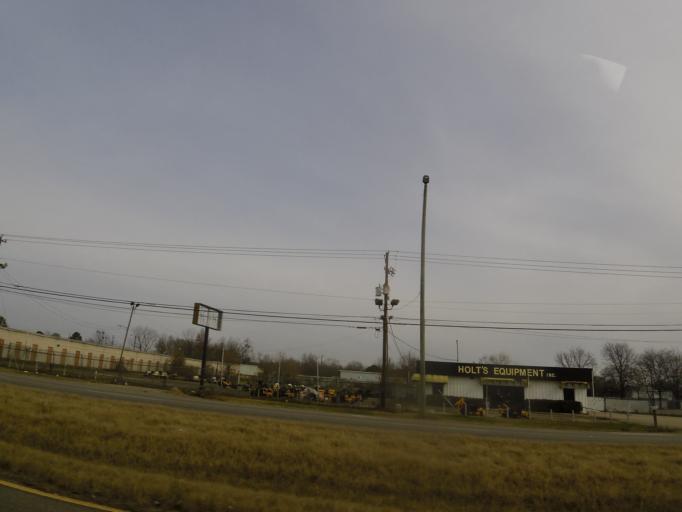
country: US
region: Alabama
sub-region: Montgomery County
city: Montgomery
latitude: 32.3185
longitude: -86.2329
